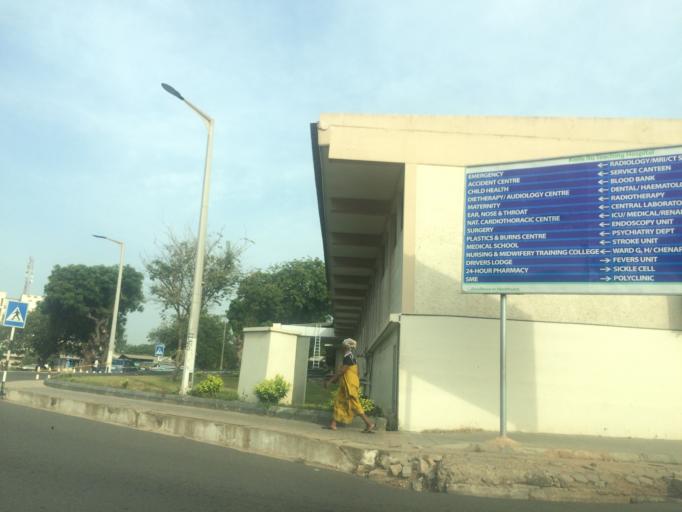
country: GH
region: Greater Accra
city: Accra
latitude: 5.5369
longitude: -0.2261
